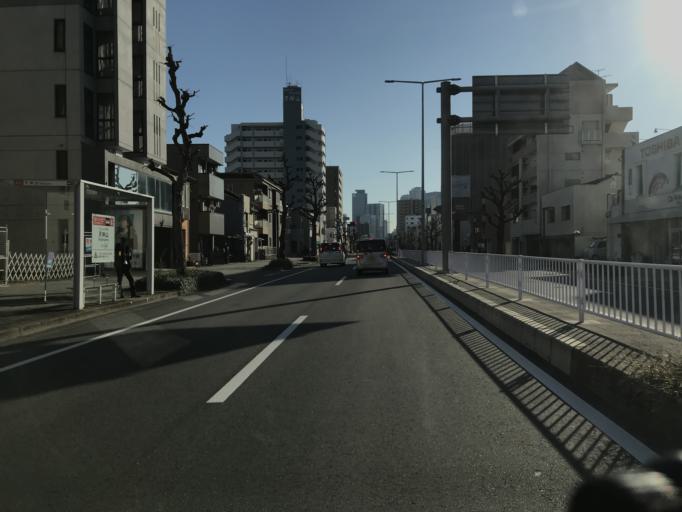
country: JP
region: Aichi
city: Nagoya-shi
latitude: 35.1914
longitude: 136.8871
